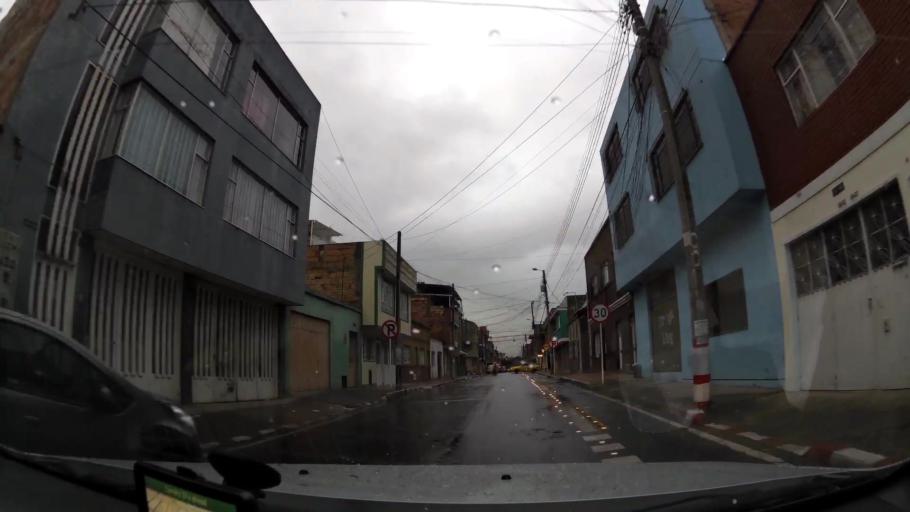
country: CO
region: Bogota D.C.
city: Bogota
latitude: 4.5867
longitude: -74.1401
